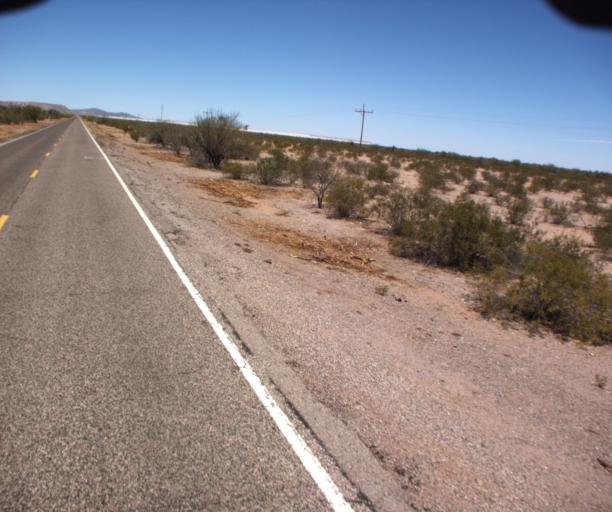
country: US
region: Arizona
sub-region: Pima County
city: Ajo
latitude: 32.3335
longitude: -112.7890
